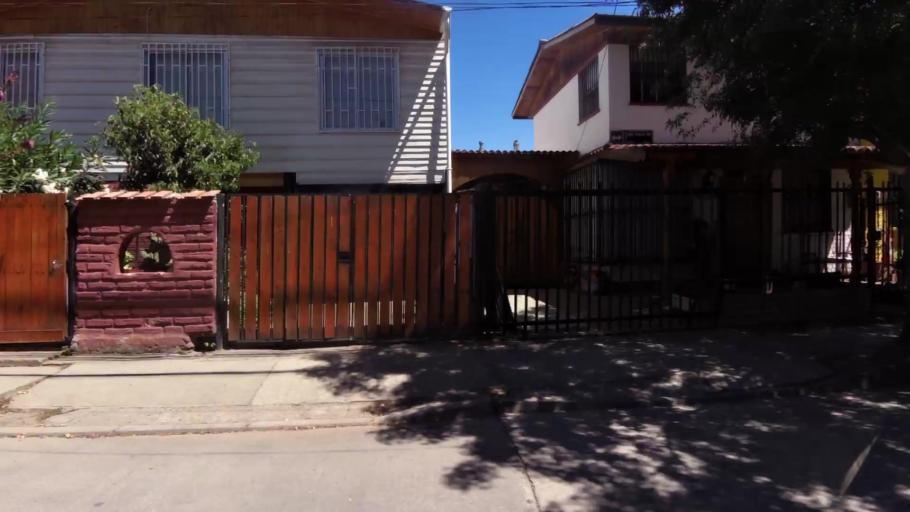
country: CL
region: O'Higgins
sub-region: Provincia de Cachapoal
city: Rancagua
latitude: -34.1561
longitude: -70.7494
